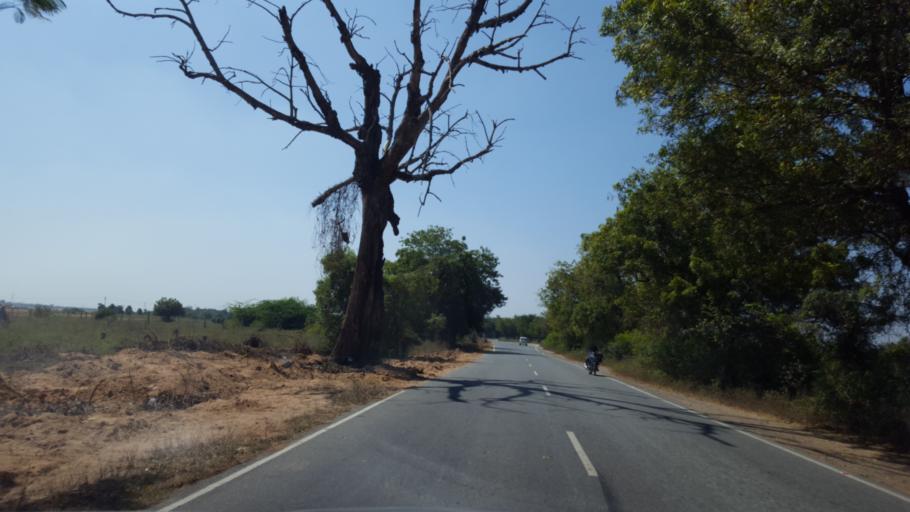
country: IN
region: Tamil Nadu
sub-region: Kancheepuram
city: Wallajahbad
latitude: 12.7738
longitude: 79.8861
